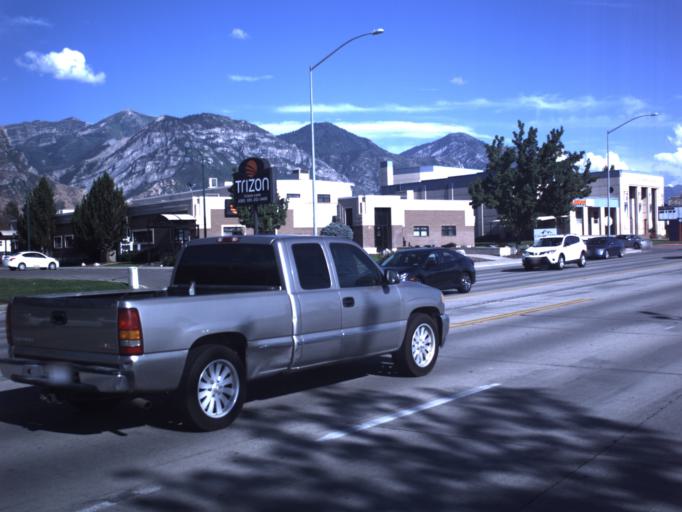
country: US
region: Utah
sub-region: Utah County
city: Orem
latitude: 40.2847
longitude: -111.6897
